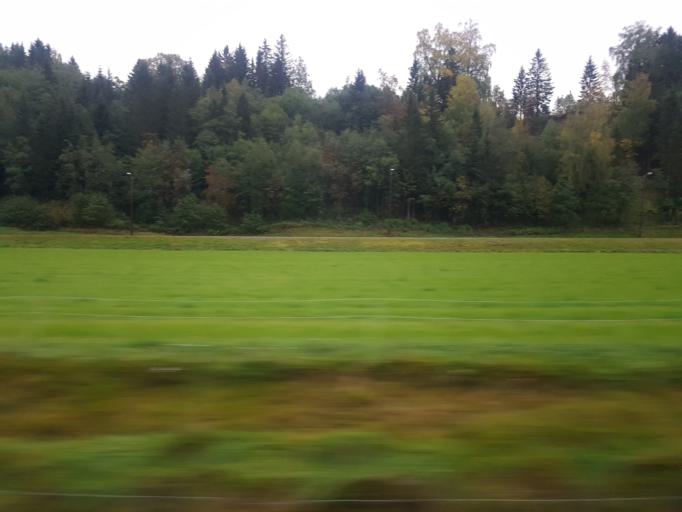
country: NO
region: Sor-Trondelag
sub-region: Melhus
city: Lundamo
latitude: 63.1411
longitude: 10.2638
